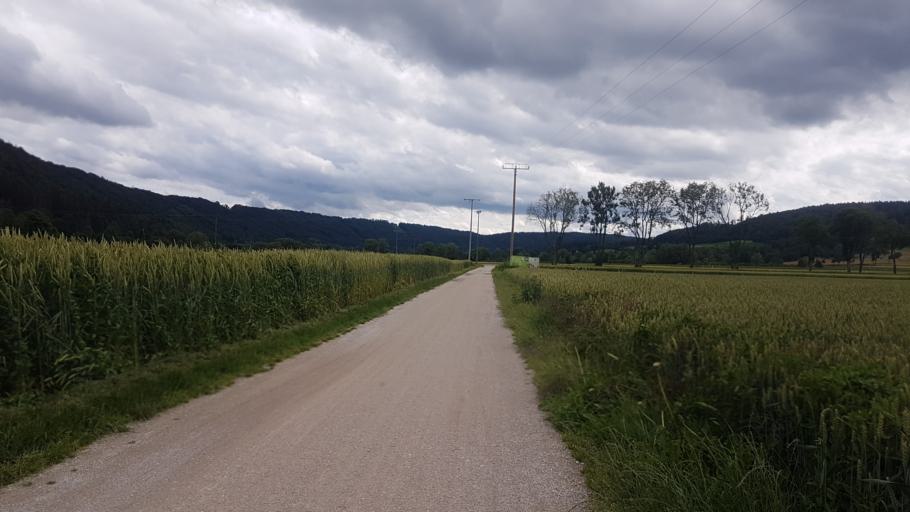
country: DE
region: Bavaria
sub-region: Upper Bavaria
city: Denkendorf
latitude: 49.0198
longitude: 11.4526
